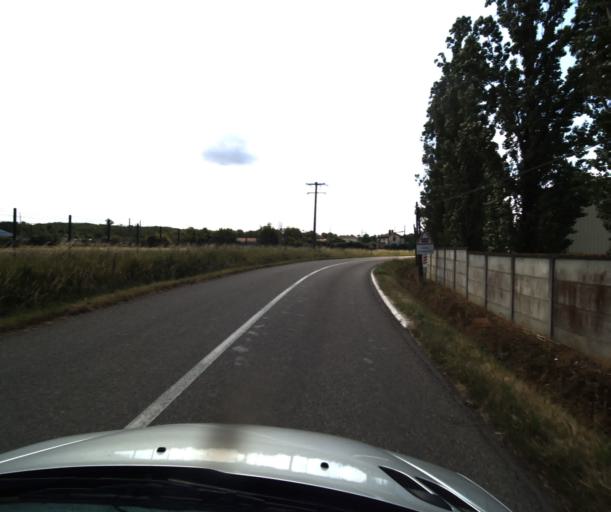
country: FR
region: Midi-Pyrenees
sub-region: Departement du Tarn-et-Garonne
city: Finhan
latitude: 43.9236
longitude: 1.2621
